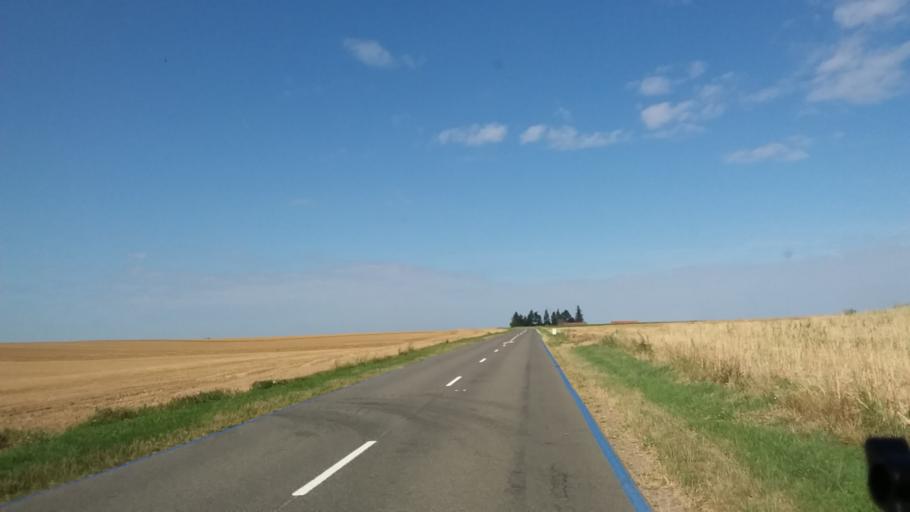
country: FR
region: Picardie
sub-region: Departement de l'Aisne
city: Bruyeres-et-Montberault
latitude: 49.4414
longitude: 3.7220
